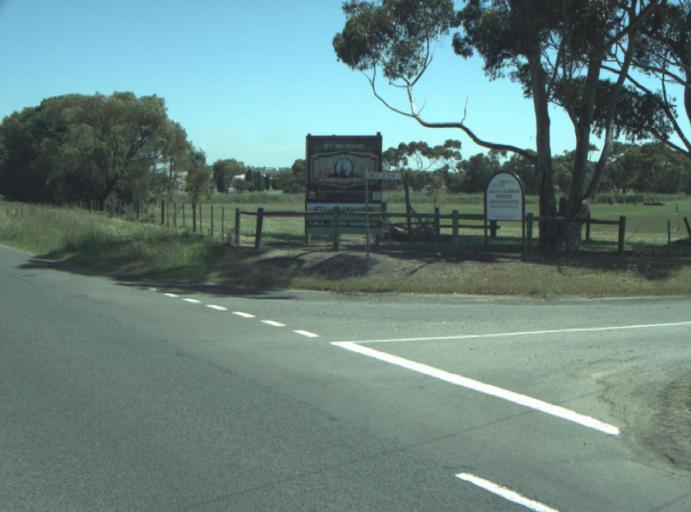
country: AU
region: Victoria
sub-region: Greater Geelong
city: Breakwater
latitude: -38.1878
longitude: 144.3557
